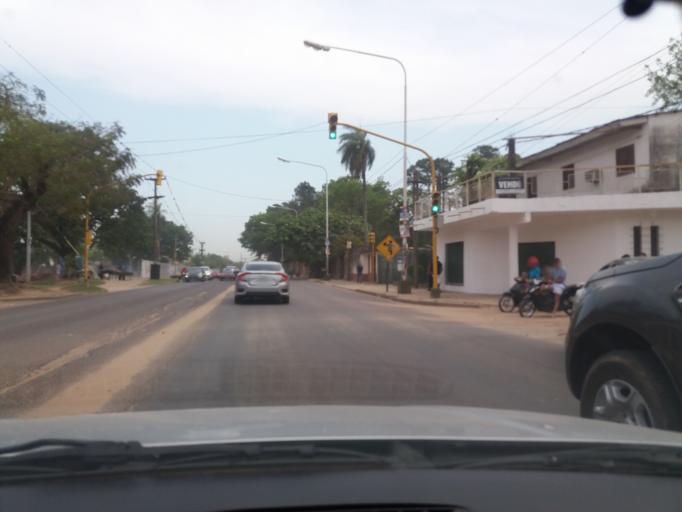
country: AR
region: Corrientes
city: Corrientes
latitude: -27.5022
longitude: -58.8127
